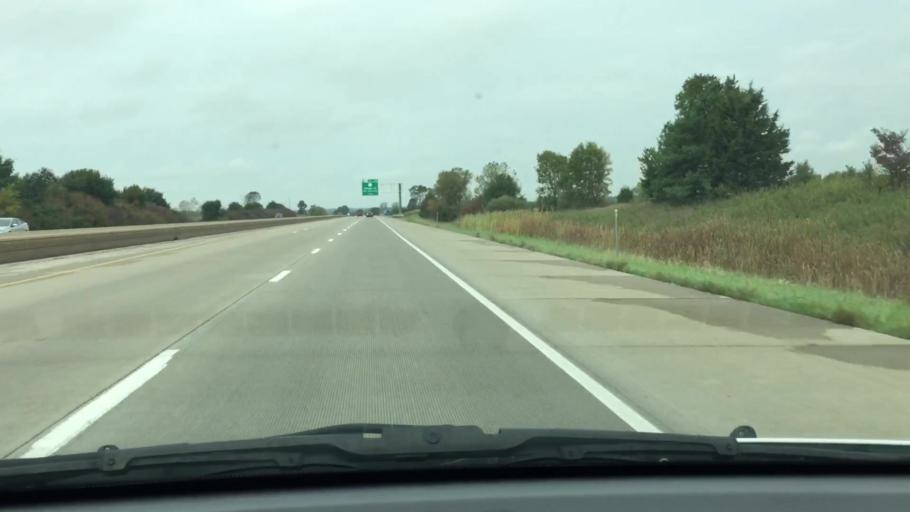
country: US
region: Iowa
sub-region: Johnson County
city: Iowa City
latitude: 41.6818
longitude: -91.4725
